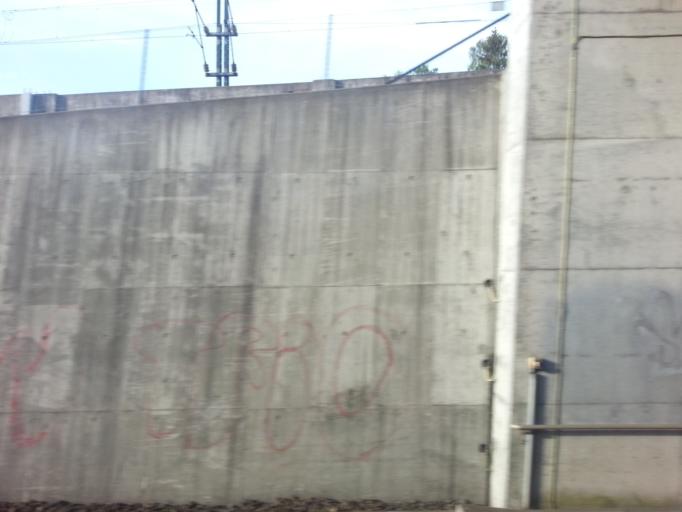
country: NO
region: Akershus
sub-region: Skedsmo
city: Lillestrom
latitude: 59.9525
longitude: 11.0329
